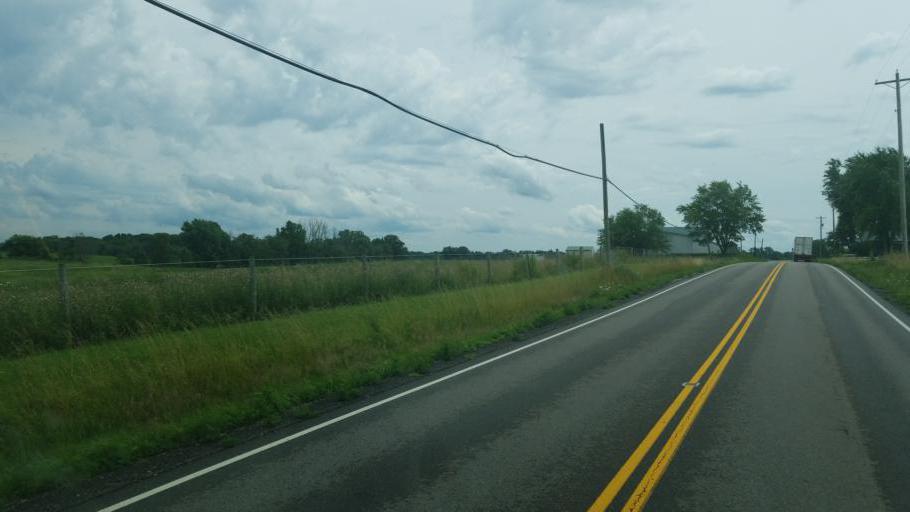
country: US
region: Ohio
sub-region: Knox County
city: Mount Vernon
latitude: 40.3430
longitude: -82.5050
